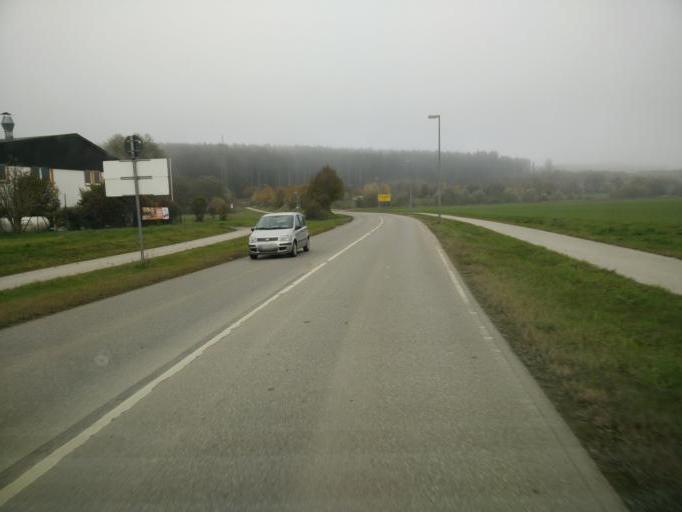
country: DE
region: Bavaria
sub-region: Swabia
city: Kaufbeuren
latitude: 47.8988
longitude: 10.6158
